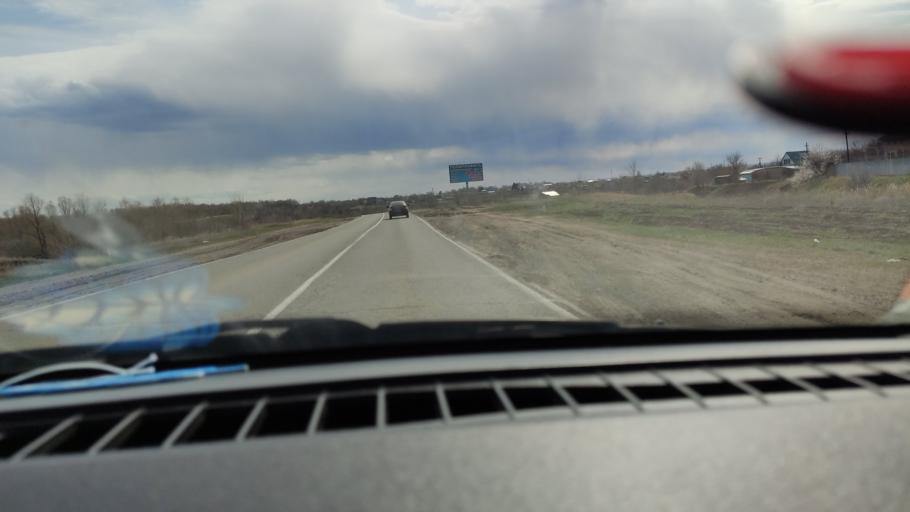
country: RU
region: Saratov
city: Privolzhskiy
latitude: 51.3475
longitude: 46.0444
